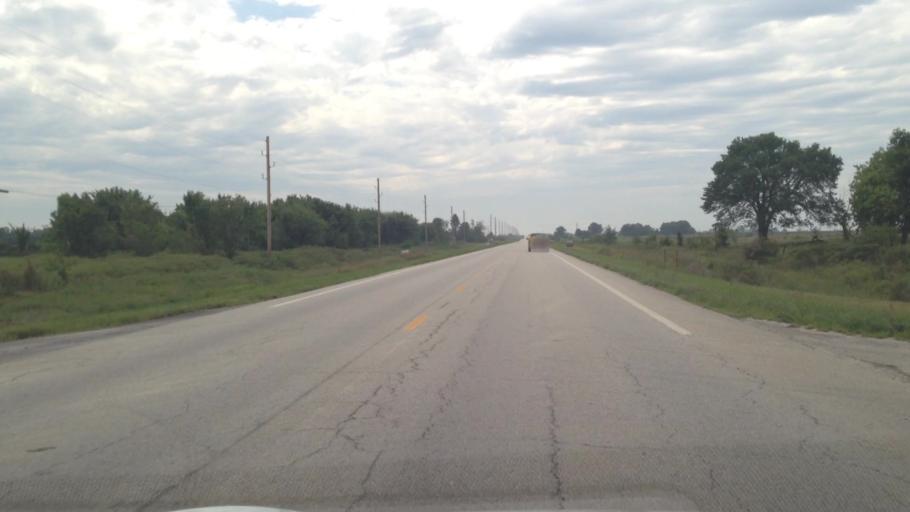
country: US
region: Kansas
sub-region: Allen County
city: Iola
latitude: 37.9506
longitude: -95.1700
